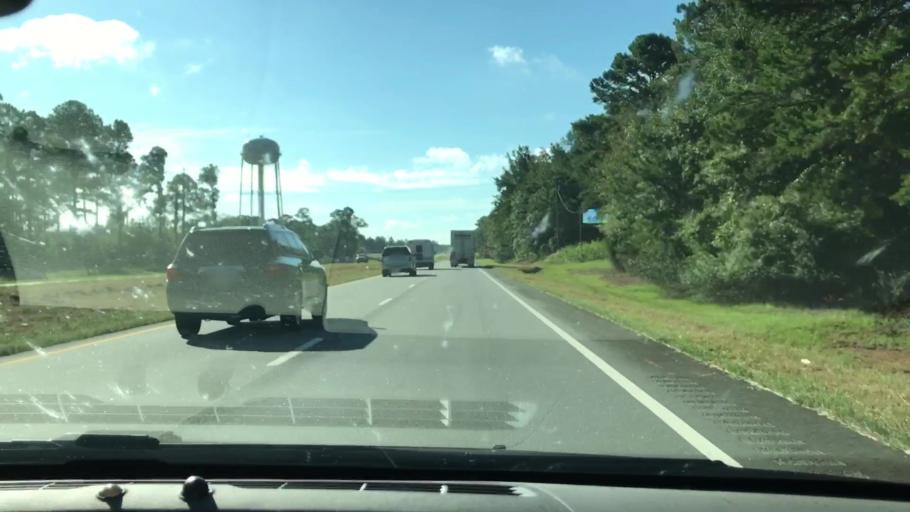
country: US
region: Georgia
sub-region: Dougherty County
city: Albany
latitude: 31.6420
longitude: -84.2540
